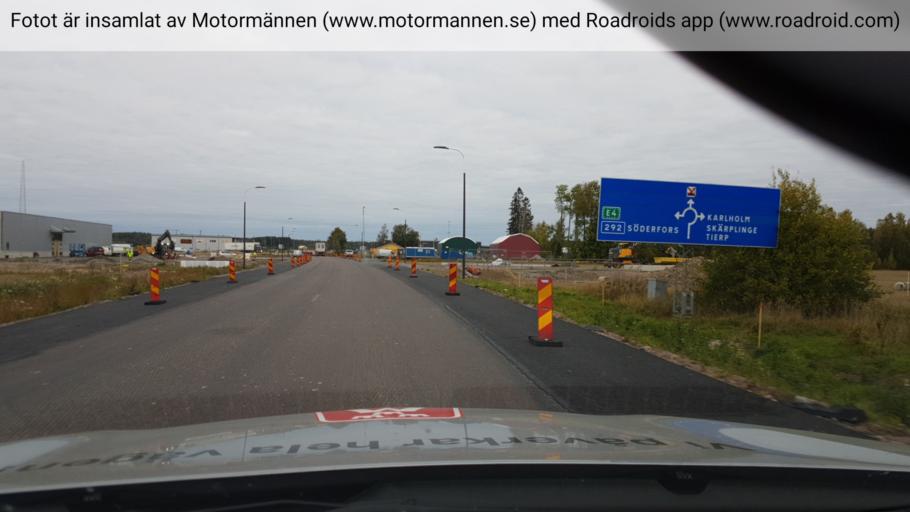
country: SE
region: Uppsala
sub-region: Tierps Kommun
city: Tierp
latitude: 60.3438
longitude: 17.4962
